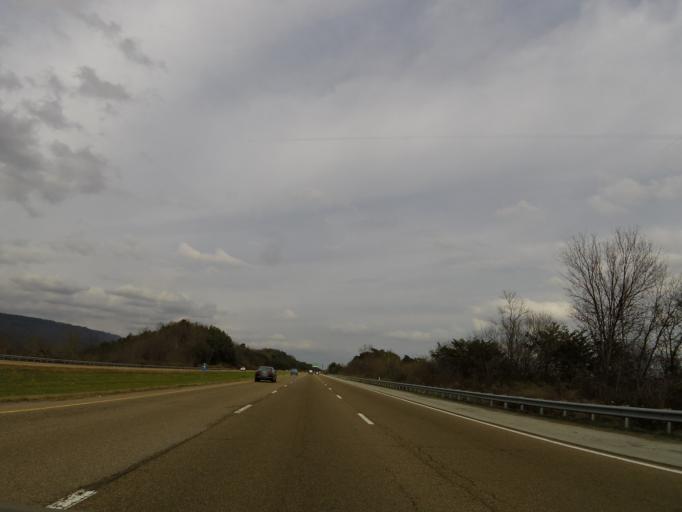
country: US
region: Tennessee
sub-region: Hamilton County
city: Red Bank
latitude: 35.1032
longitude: -85.3145
